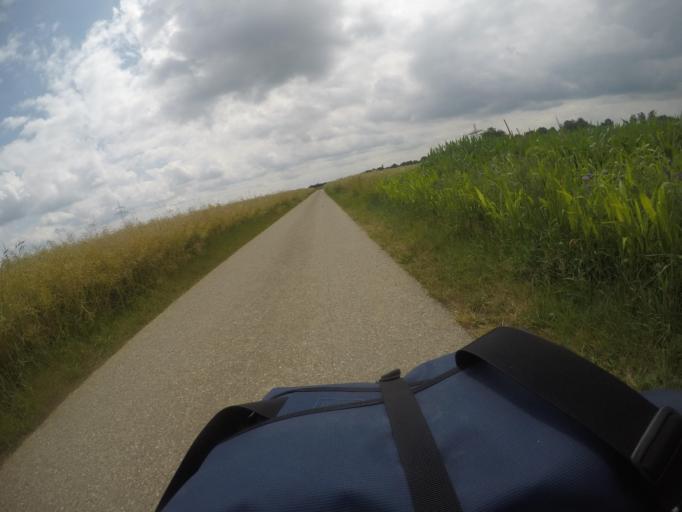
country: DE
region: Bavaria
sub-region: Swabia
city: Heimertingen
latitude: 48.0534
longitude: 10.1563
